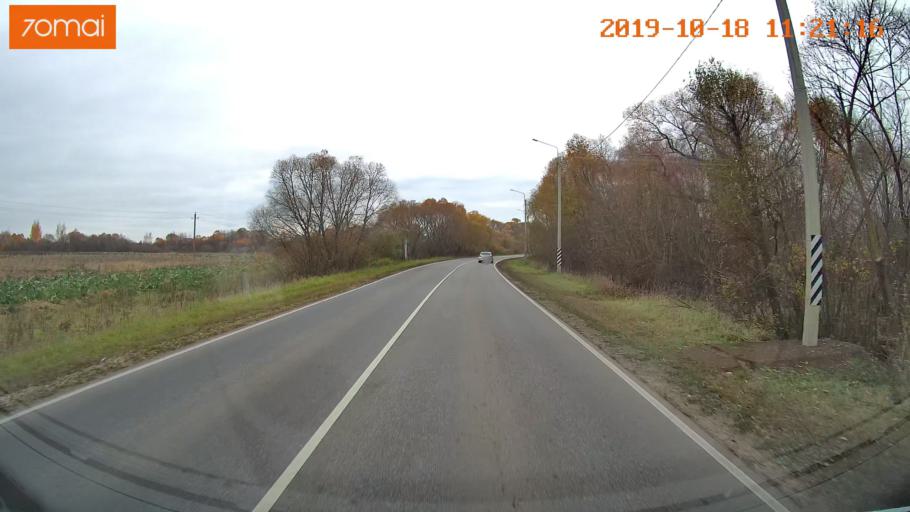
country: RU
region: Tula
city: Kimovsk
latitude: 54.0721
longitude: 38.5633
